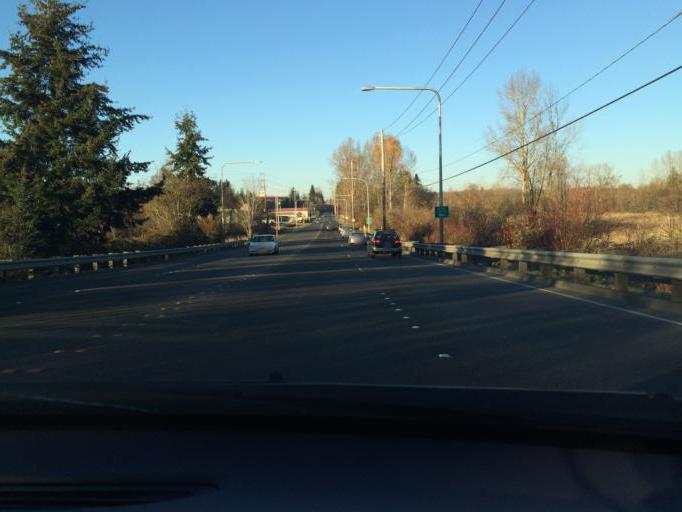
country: US
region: Washington
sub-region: Whatcom County
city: Bellingham
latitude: 48.7792
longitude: -122.4426
